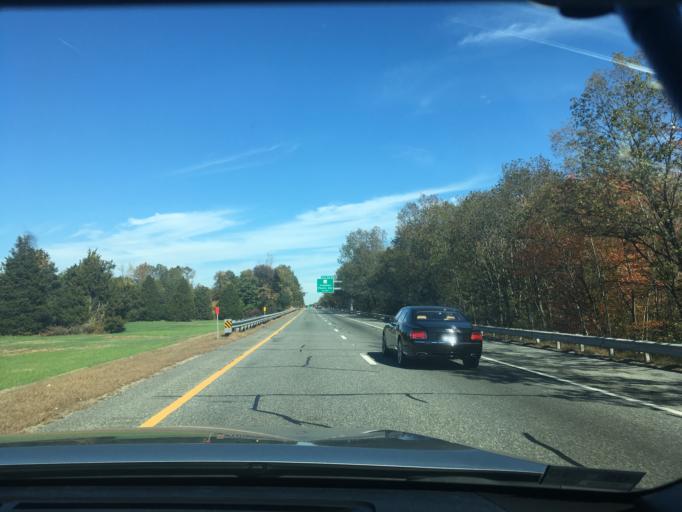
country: US
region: Rhode Island
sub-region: Kent County
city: West Warwick
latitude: 41.7440
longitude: -71.4865
